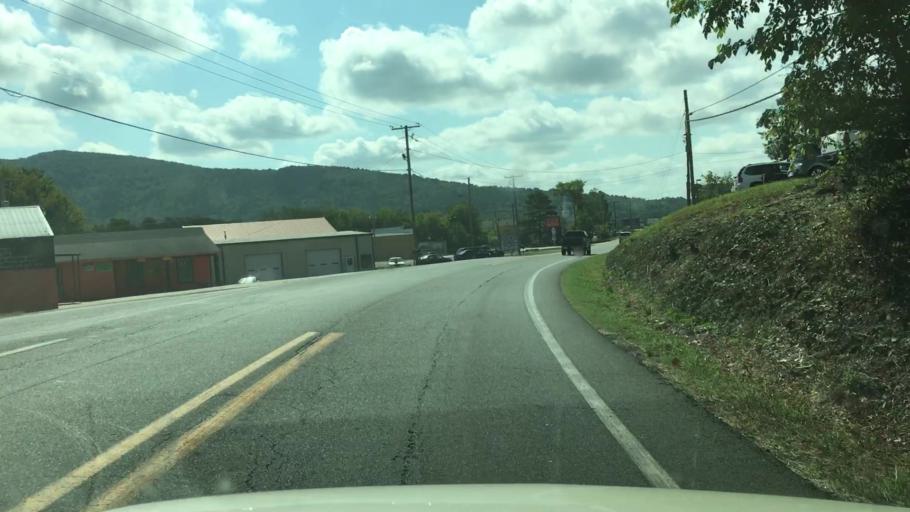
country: US
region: Arkansas
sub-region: Garland County
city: Piney
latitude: 34.5072
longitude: -93.1308
